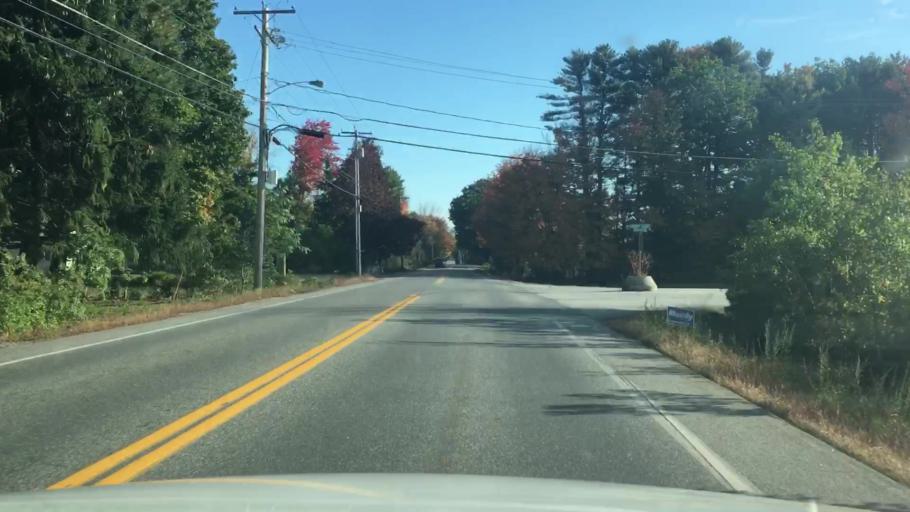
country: US
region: Maine
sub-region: Cumberland County
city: Gorham
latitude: 43.6260
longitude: -70.4556
